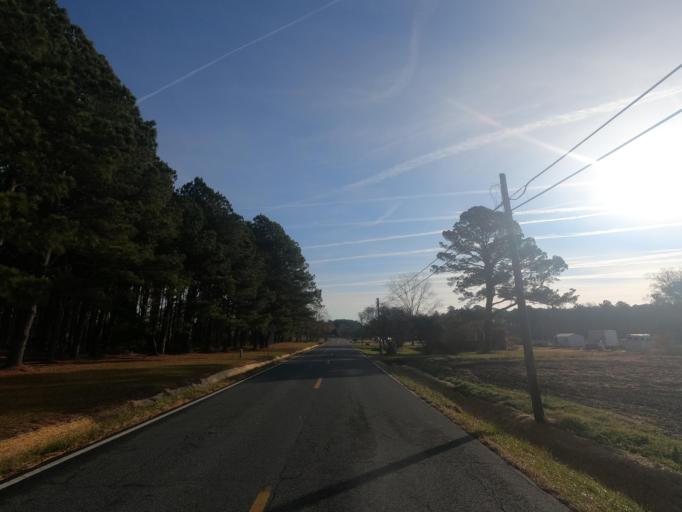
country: US
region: Maryland
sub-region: Somerset County
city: Crisfield
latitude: 38.0335
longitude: -75.7841
